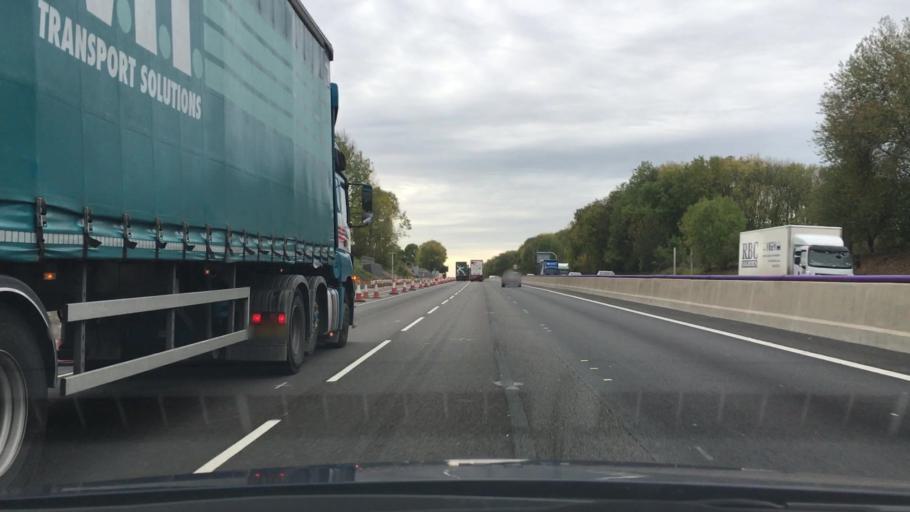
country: GB
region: England
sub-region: Northamptonshire
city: Long Buckby
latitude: 52.3381
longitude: -1.1501
